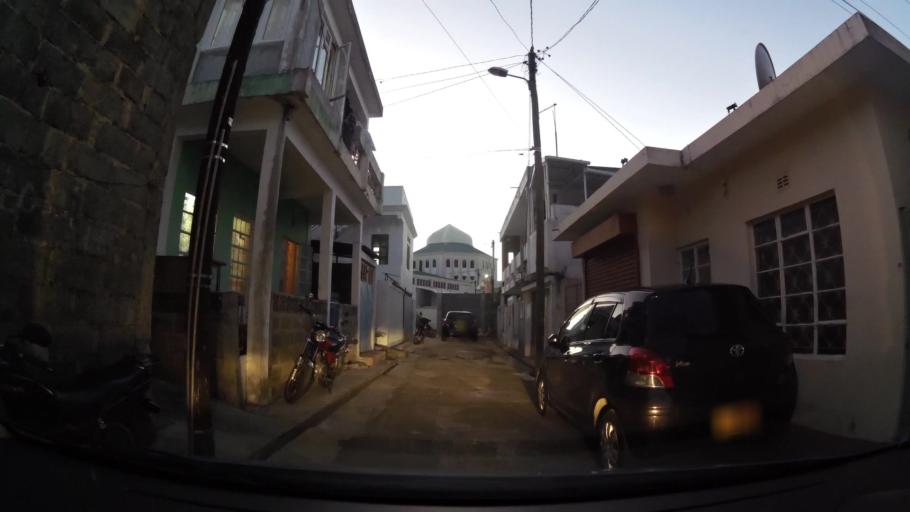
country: MU
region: Port Louis
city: Port Louis
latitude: -20.1644
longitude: 57.5130
